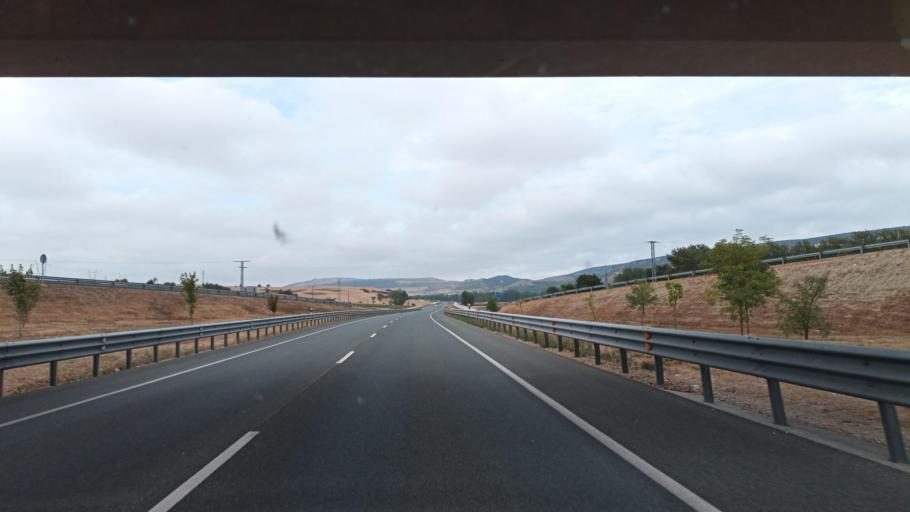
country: ES
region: Castille and Leon
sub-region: Provincia de Burgos
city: Castil de Peones
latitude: 42.4800
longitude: -3.3977
